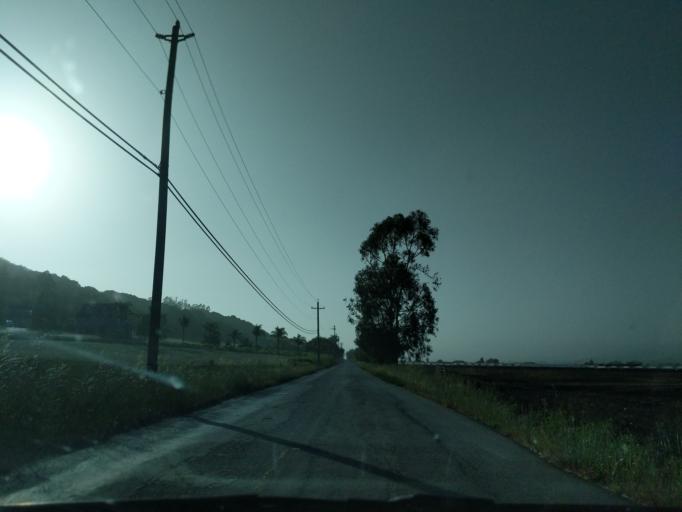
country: US
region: California
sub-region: San Benito County
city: Aromas
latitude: 36.8869
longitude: -121.6850
